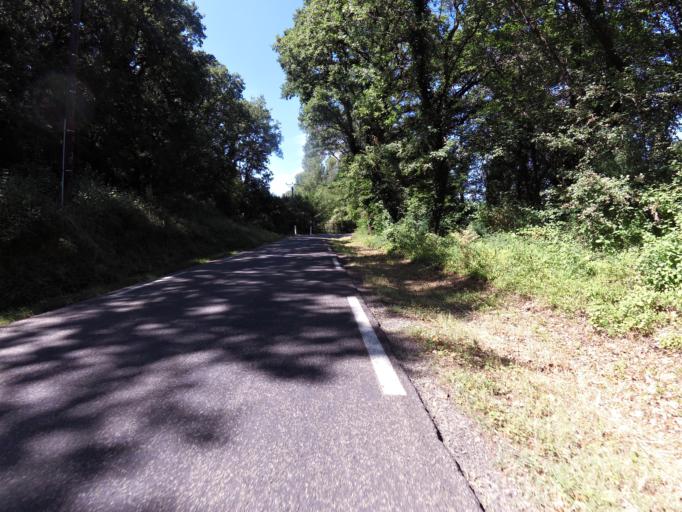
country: FR
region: Languedoc-Roussillon
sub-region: Departement du Gard
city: Sommieres
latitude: 43.8283
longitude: 4.0652
